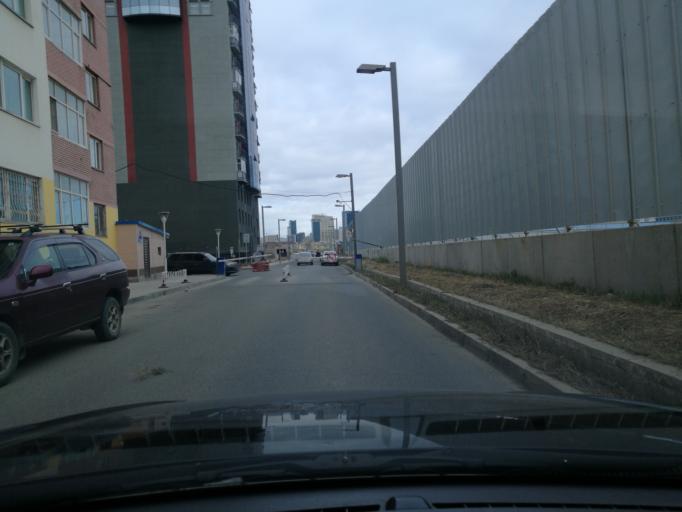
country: MN
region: Ulaanbaatar
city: Ulaanbaatar
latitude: 47.9011
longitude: 106.9208
